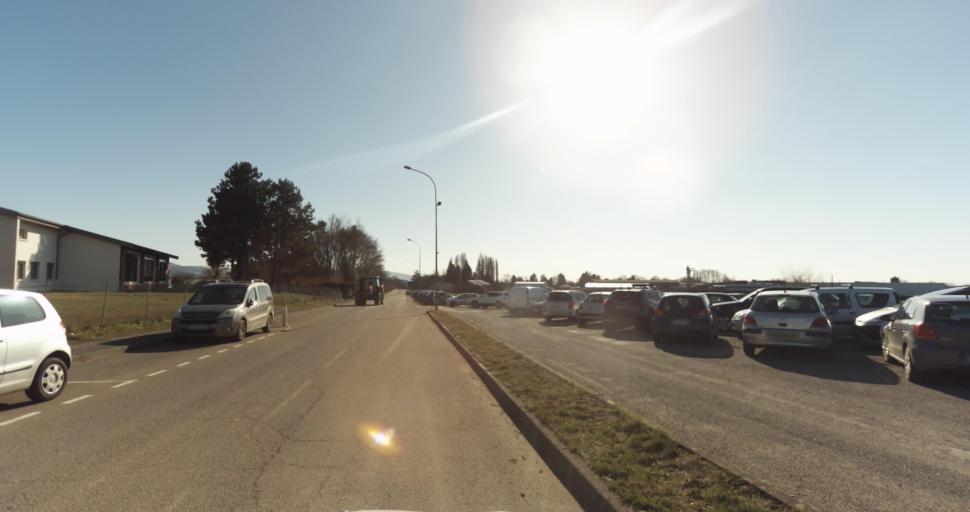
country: FR
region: Franche-Comte
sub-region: Departement du Jura
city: Montmorot
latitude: 46.6894
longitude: 5.5098
